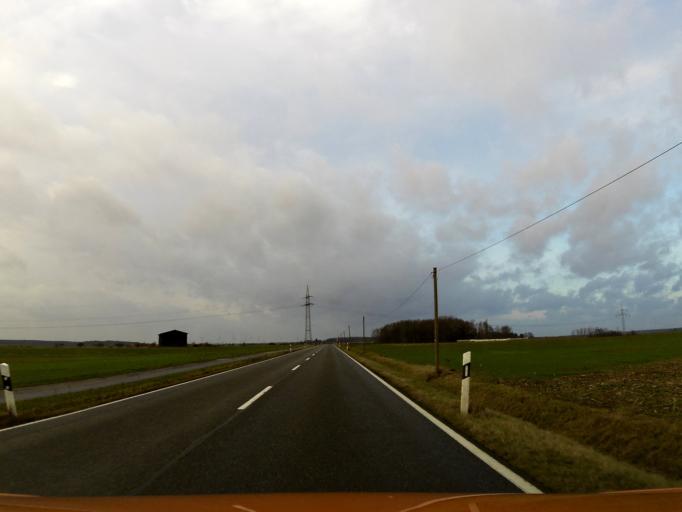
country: DE
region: Lower Saxony
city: Gross Twulpstedt
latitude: 52.3522
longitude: 10.9383
